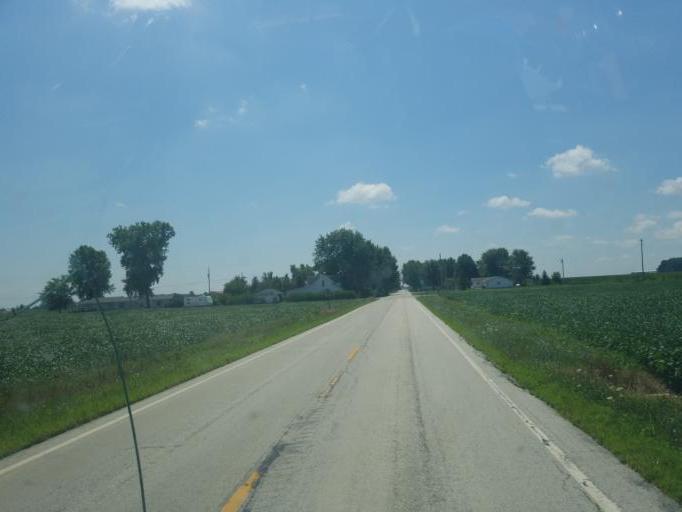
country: US
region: Ohio
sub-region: Allen County
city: Spencerville
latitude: 40.7005
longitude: -84.4256
